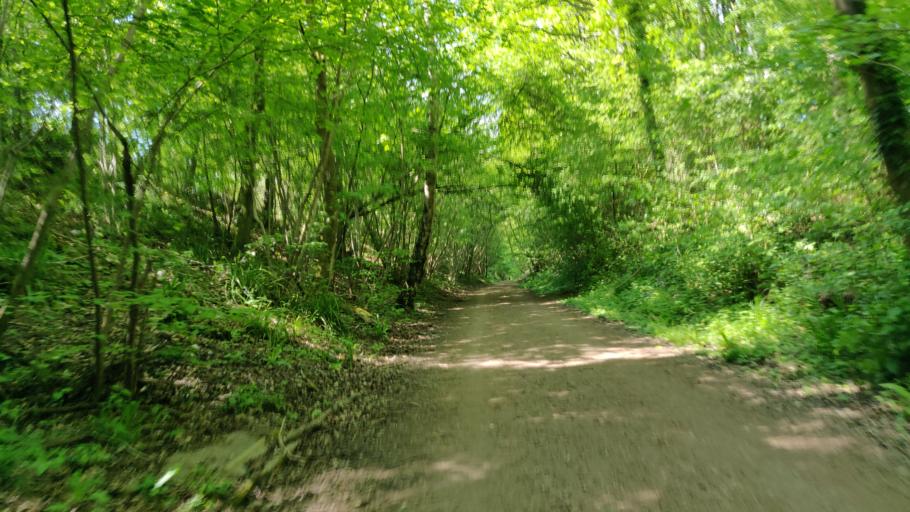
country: GB
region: England
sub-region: West Sussex
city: Rudgwick
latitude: 51.0714
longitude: -0.4224
